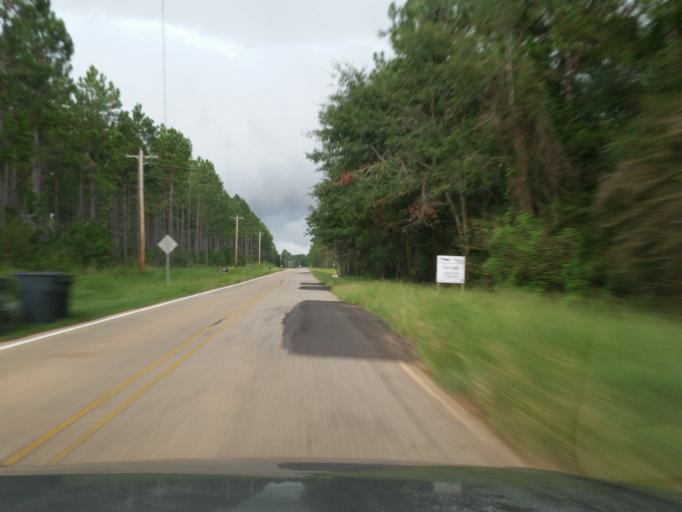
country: US
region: Alabama
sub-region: Baldwin County
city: Robertsdale
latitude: 30.5863
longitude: -87.5646
